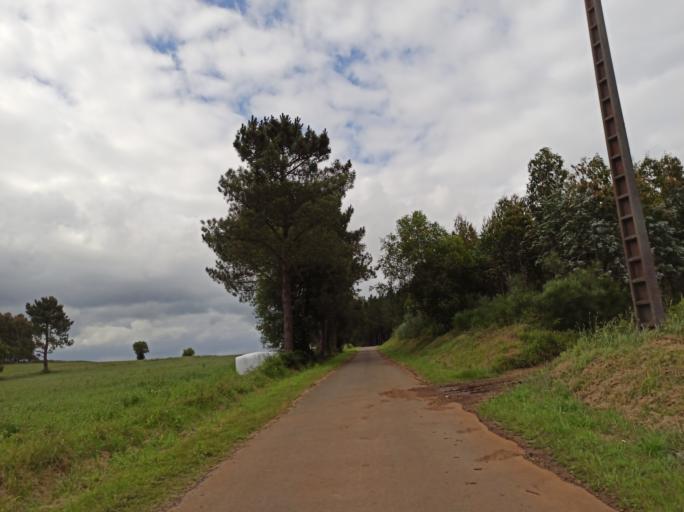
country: ES
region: Galicia
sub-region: Provincia de Pontevedra
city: Silleda
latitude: 42.7608
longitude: -8.1602
